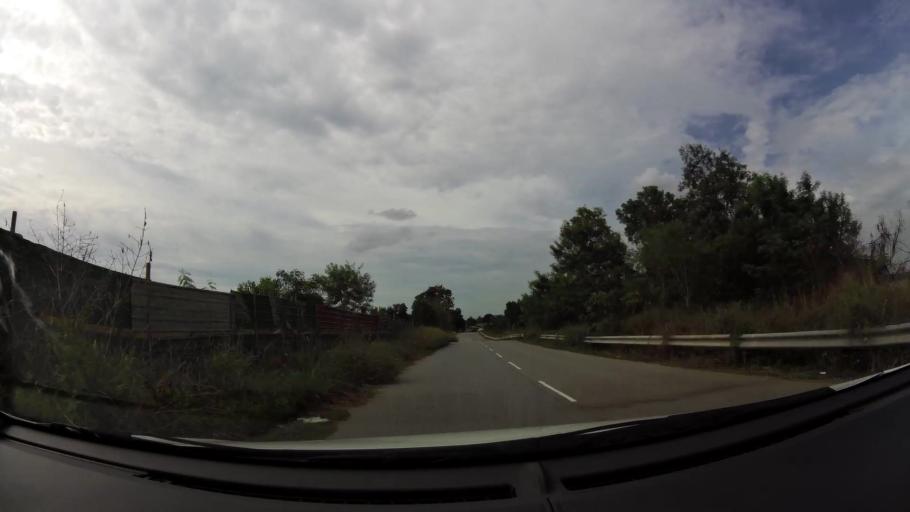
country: BN
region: Brunei and Muara
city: Bandar Seri Begawan
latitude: 4.8937
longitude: 114.8951
